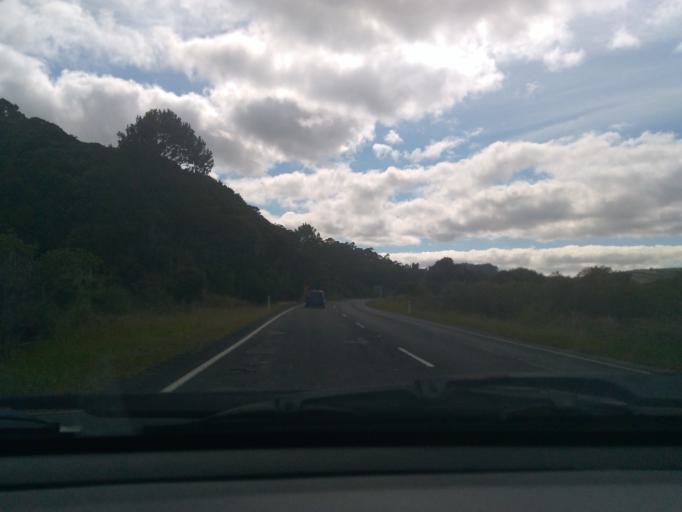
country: NZ
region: Northland
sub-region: Far North District
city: Taipa
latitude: -35.0114
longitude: 173.5469
